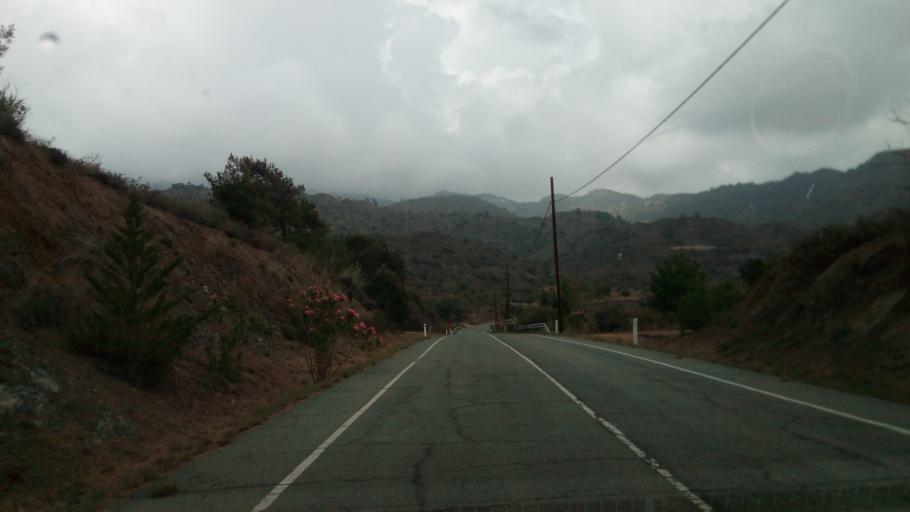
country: CY
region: Limassol
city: Parekklisha
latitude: 34.8664
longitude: 33.1885
